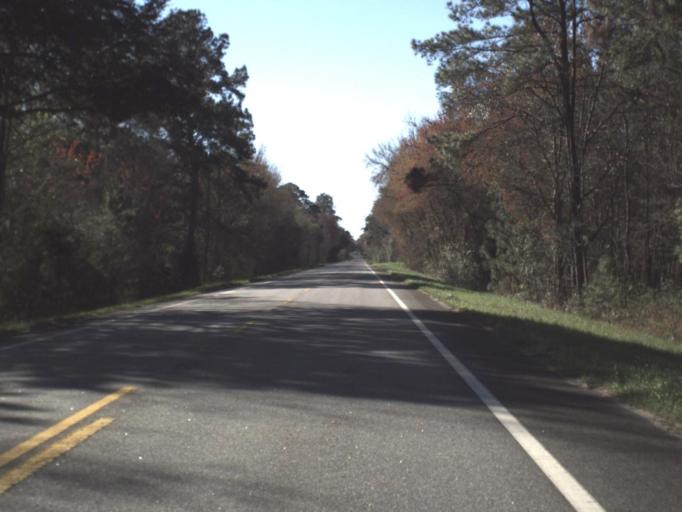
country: US
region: Georgia
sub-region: Brooks County
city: Quitman
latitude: 30.5967
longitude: -83.6426
